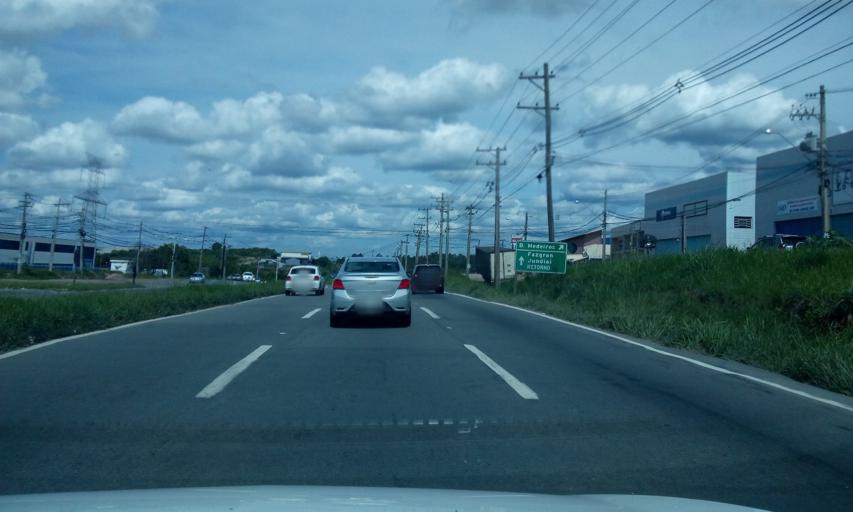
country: BR
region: Sao Paulo
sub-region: Itupeva
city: Itupeva
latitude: -23.1675
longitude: -47.0057
